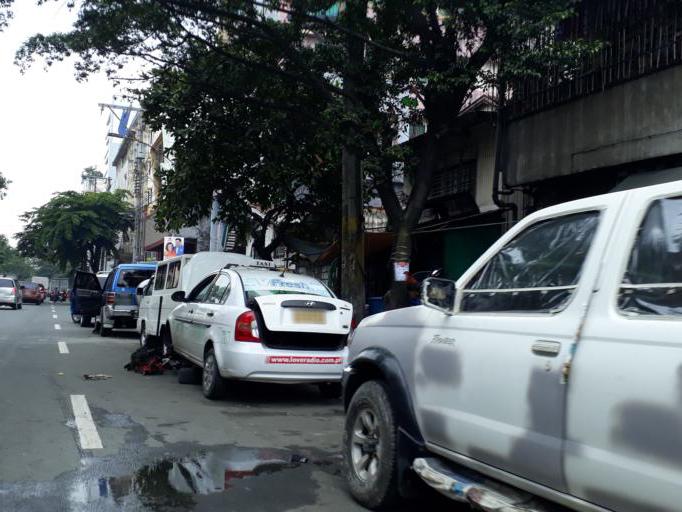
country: PH
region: Metro Manila
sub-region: City of Manila
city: Manila
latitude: 14.6224
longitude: 120.9781
